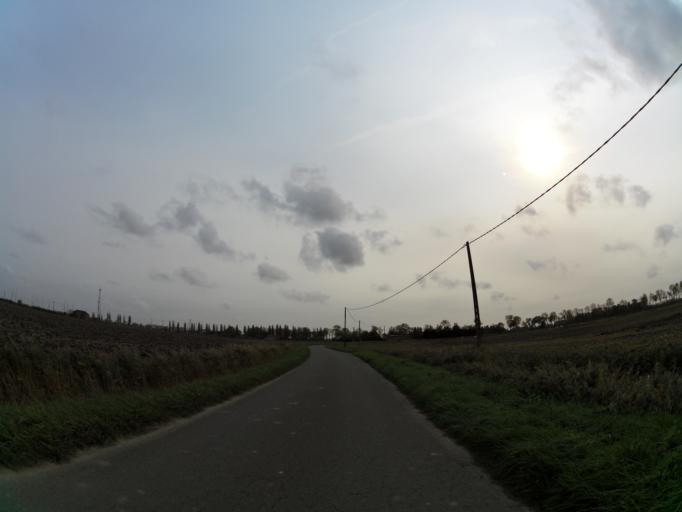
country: BE
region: Flanders
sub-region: Provincie West-Vlaanderen
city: Oudenburg
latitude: 51.2116
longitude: 3.0211
